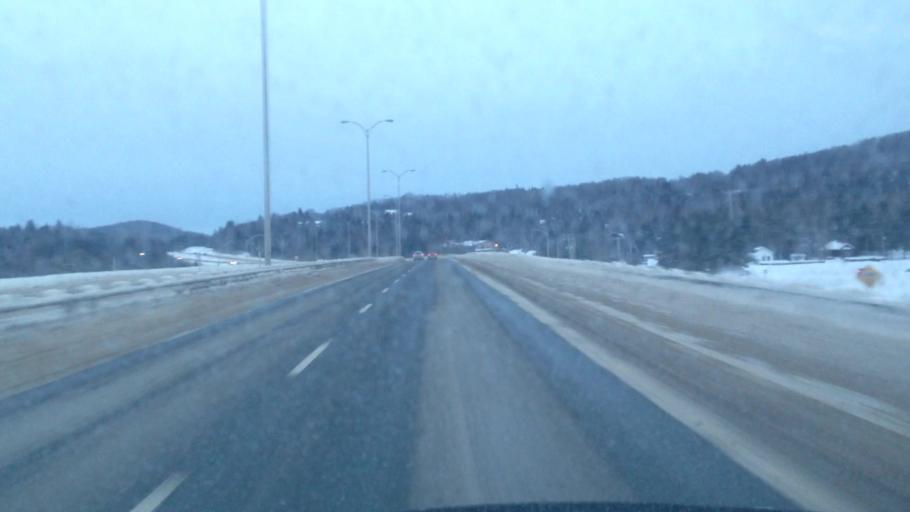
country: CA
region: Quebec
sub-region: Laurentides
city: Mont-Tremblant
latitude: 46.1100
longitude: -74.4851
